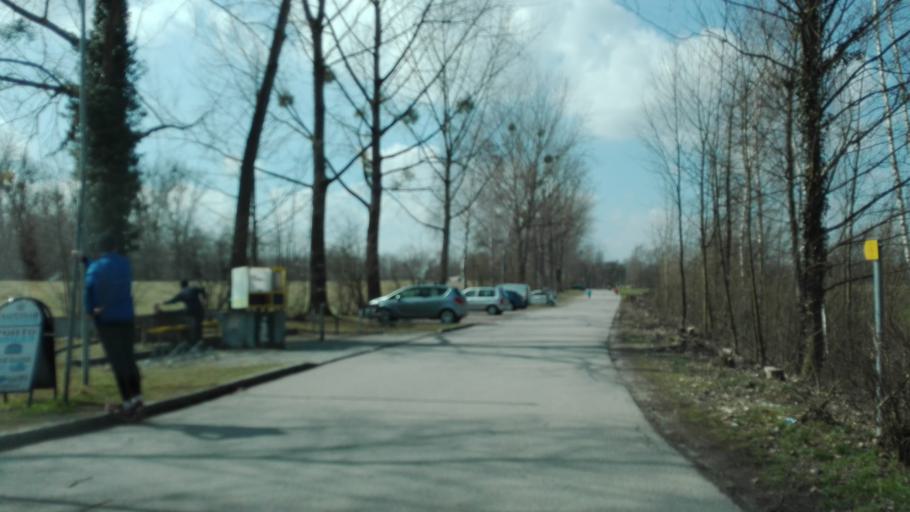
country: AT
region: Upper Austria
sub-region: Politischer Bezirk Urfahr-Umgebung
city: Ottensheim
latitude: 48.3313
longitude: 14.1702
